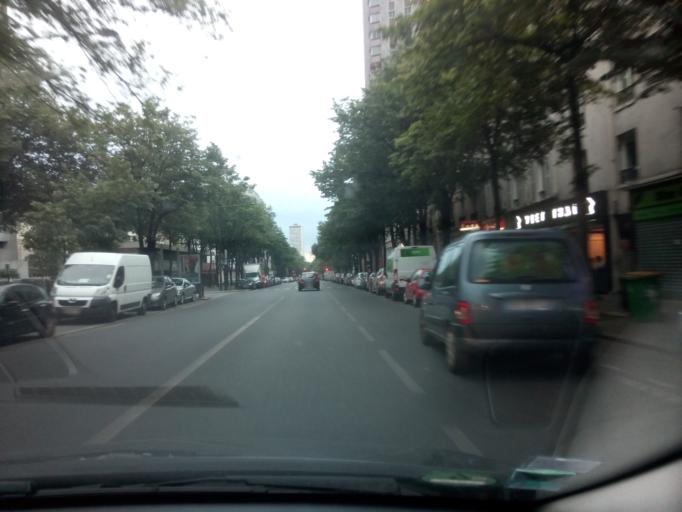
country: FR
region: Ile-de-France
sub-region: Departement du Val-de-Marne
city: Le Kremlin-Bicetre
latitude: 48.8302
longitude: 2.3567
